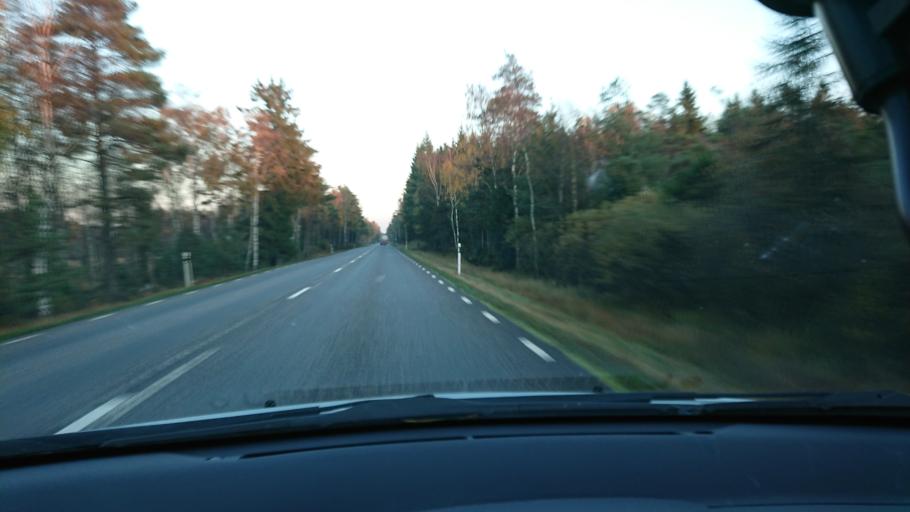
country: SE
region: Halland
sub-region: Laholms Kommun
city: Knared
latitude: 56.7148
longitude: 13.2236
